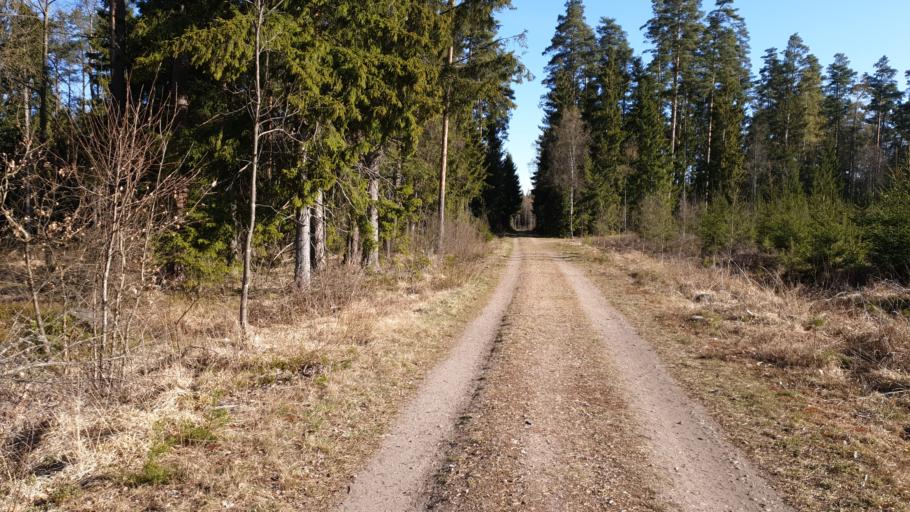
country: SE
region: Kronoberg
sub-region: Ljungby Kommun
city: Ljungby
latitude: 56.8334
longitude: 13.9038
